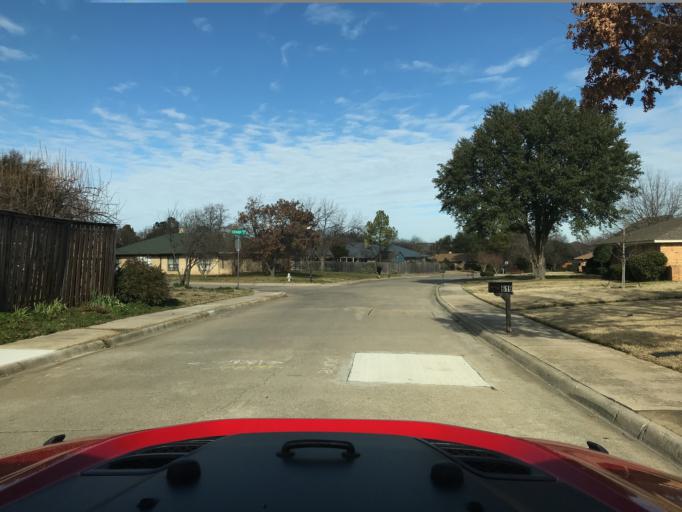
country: US
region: Texas
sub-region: Denton County
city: Lewisville
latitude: 33.0508
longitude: -97.0327
